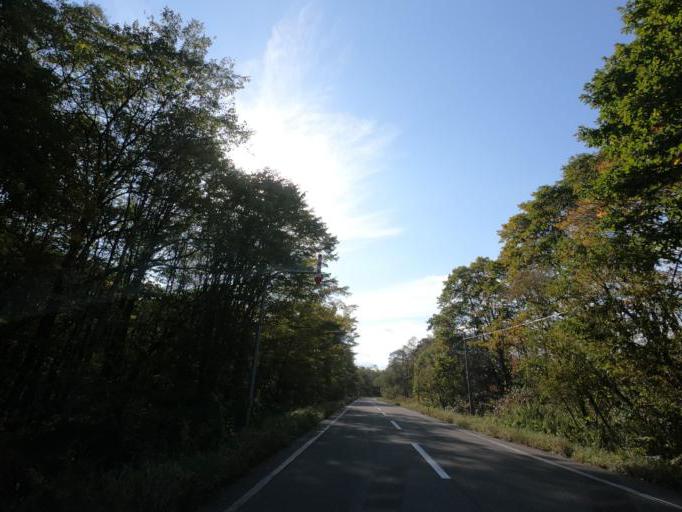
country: JP
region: Hokkaido
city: Obihiro
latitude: 42.6181
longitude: 143.4054
